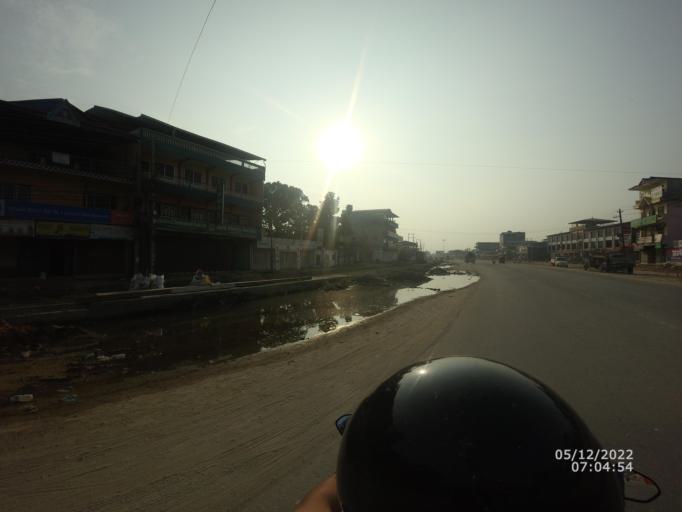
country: NP
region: Central Region
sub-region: Narayani Zone
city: Bharatpur
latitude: 27.6711
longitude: 84.4359
